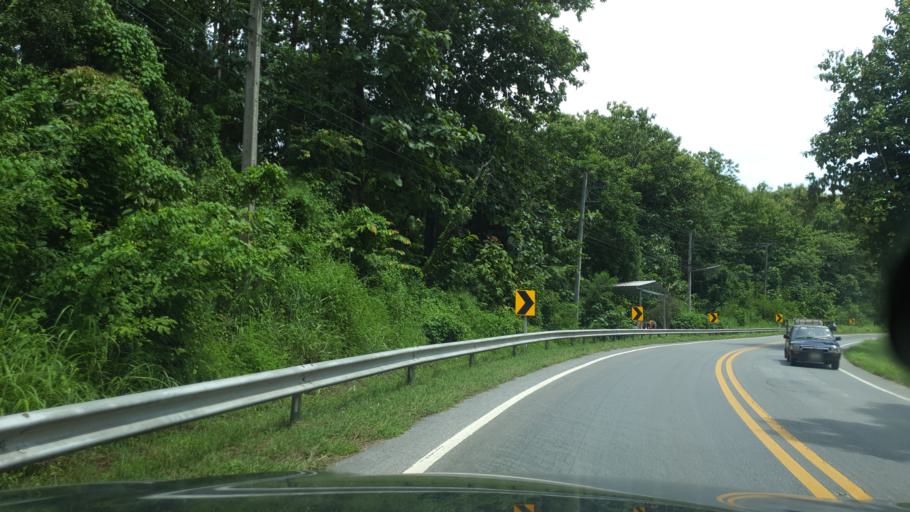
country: TH
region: Sukhothai
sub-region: Amphoe Si Satchanalai
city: Si Satchanalai
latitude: 17.6321
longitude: 99.6899
